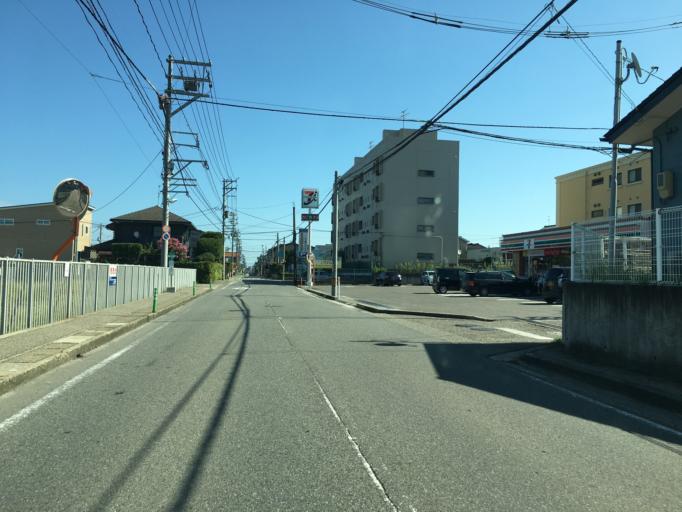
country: JP
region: Niigata
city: Niigata-shi
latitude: 37.8990
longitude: 138.9952
